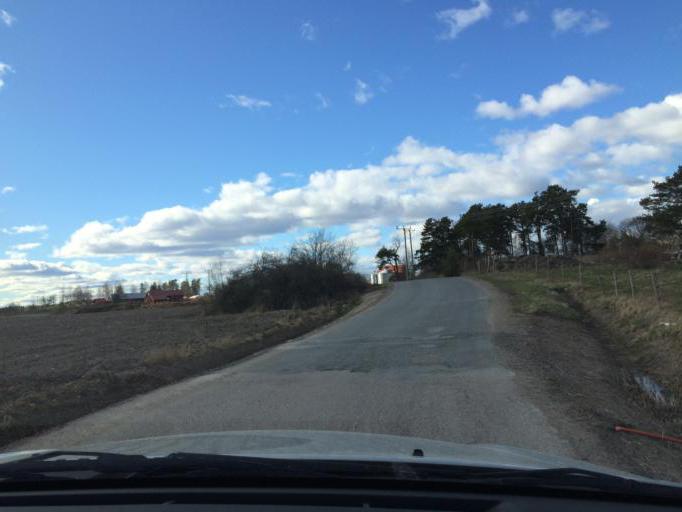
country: SE
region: Soedermanland
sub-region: Eskilstuna Kommun
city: Kvicksund
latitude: 59.4322
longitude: 16.3515
